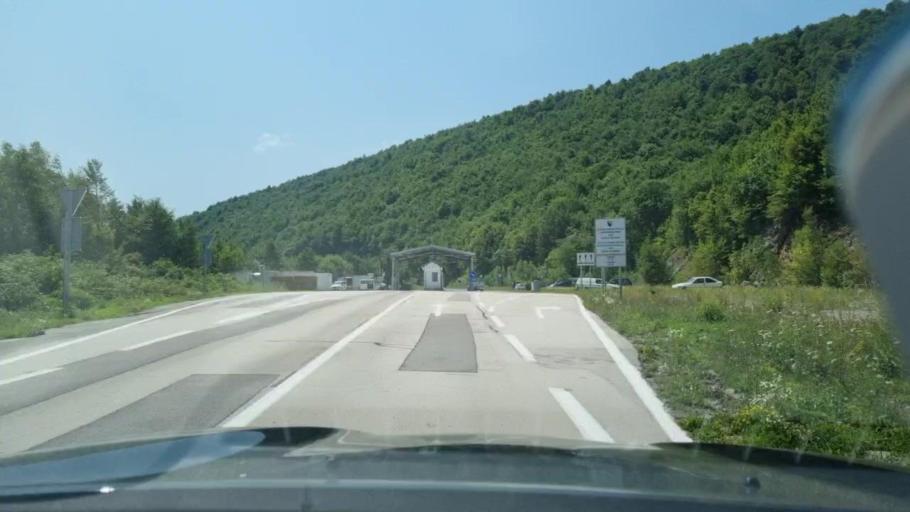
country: BA
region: Federation of Bosnia and Herzegovina
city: Bihac
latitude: 44.7149
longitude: 15.9285
